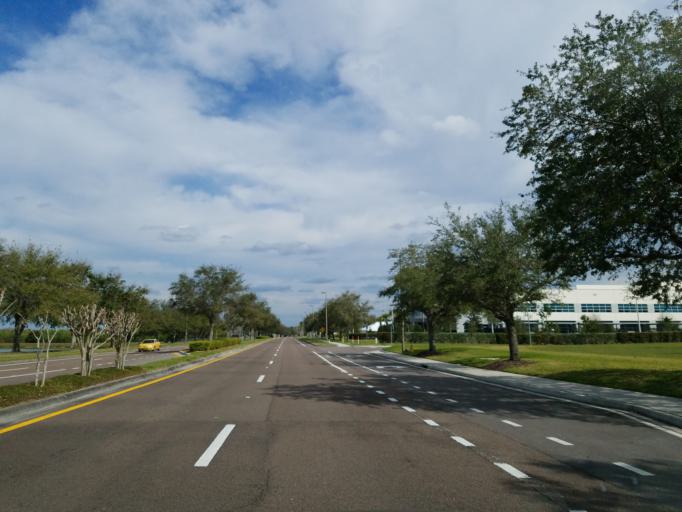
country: US
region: Florida
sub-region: Hillsborough County
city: Palm River-Clair Mel
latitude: 27.9343
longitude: -82.3484
